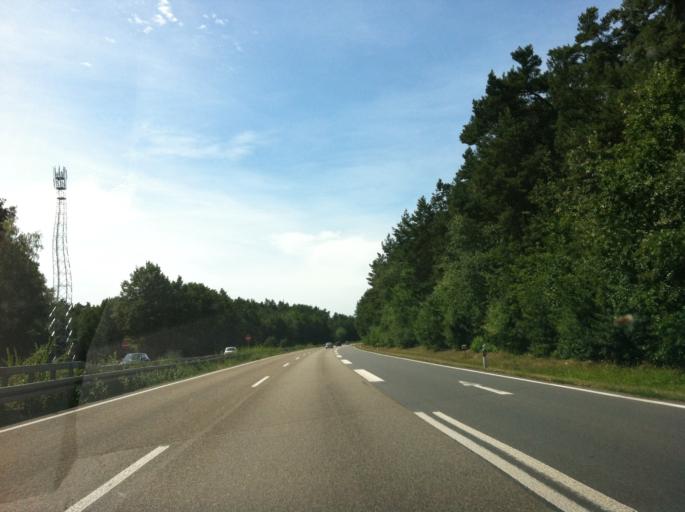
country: DE
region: Hesse
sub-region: Regierungsbezirk Darmstadt
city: Eppertshausen
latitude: 49.9652
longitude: 8.8577
